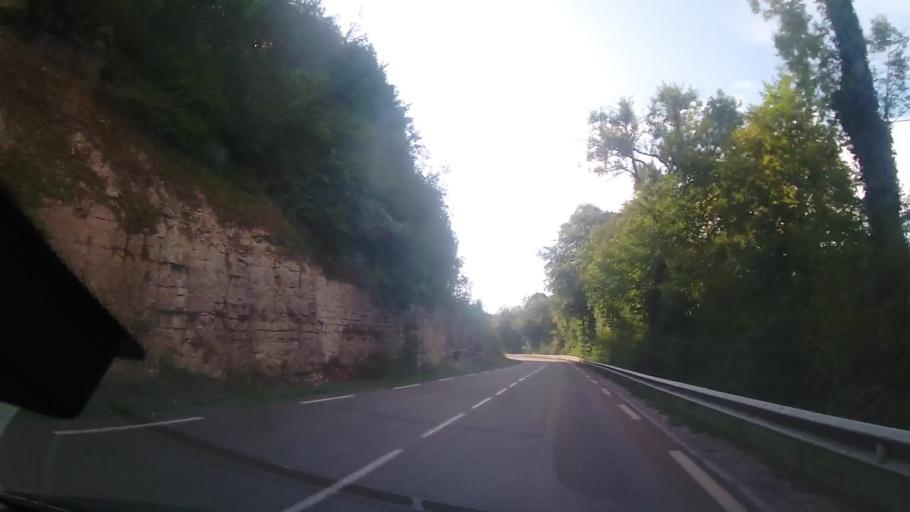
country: FR
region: Franche-Comte
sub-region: Departement du Jura
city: Clairvaux-les-Lacs
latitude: 46.5845
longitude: 5.8252
